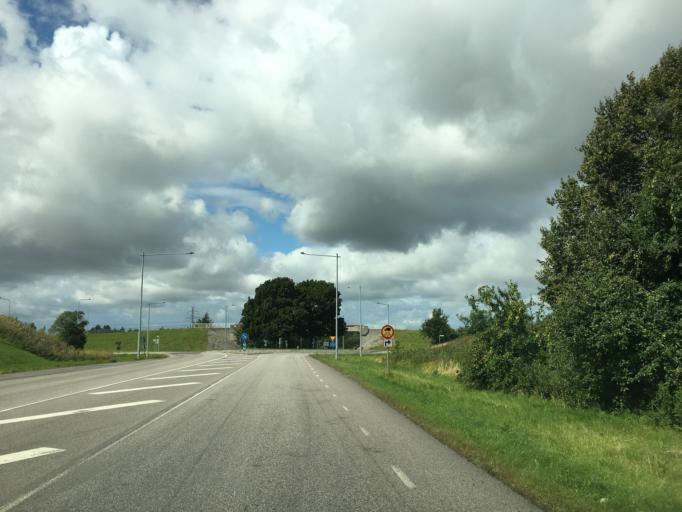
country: SE
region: Skane
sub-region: Svedala Kommun
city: Svedala
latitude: 55.5093
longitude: 13.2186
